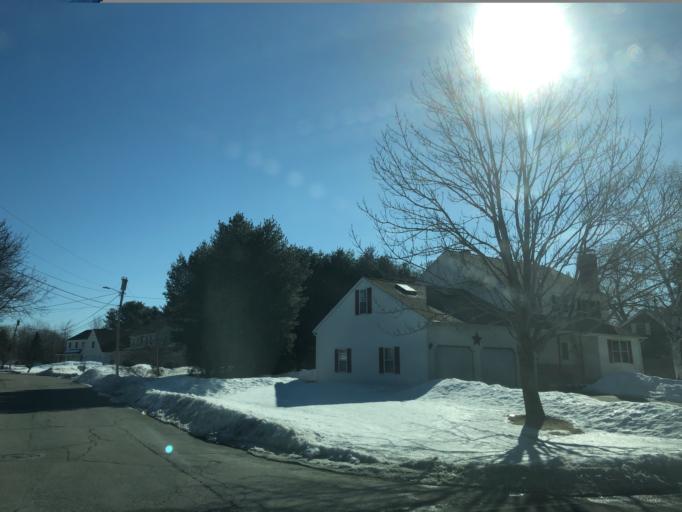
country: US
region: Maine
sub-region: Penobscot County
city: Brewer
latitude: 44.8196
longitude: -68.7502
